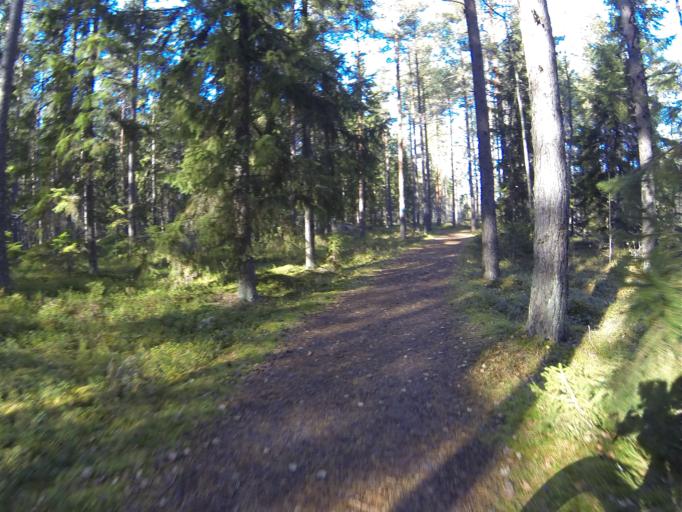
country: FI
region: Varsinais-Suomi
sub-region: Salo
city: Saerkisalo
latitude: 60.2088
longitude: 22.9204
